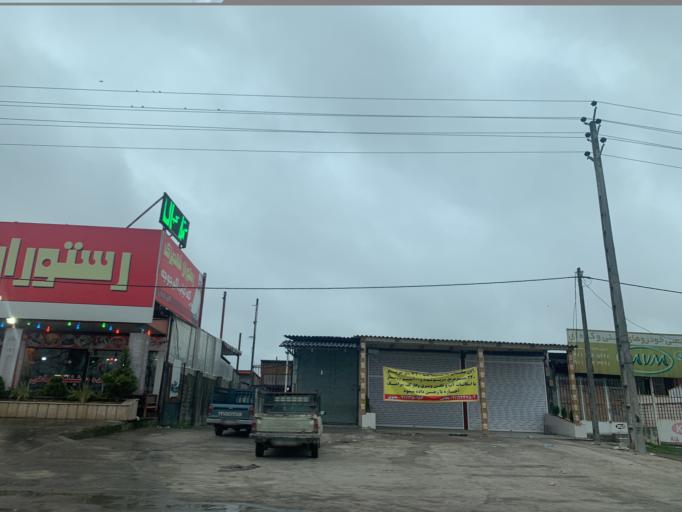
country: IR
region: Mazandaran
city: Amol
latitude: 36.4267
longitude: 52.3496
